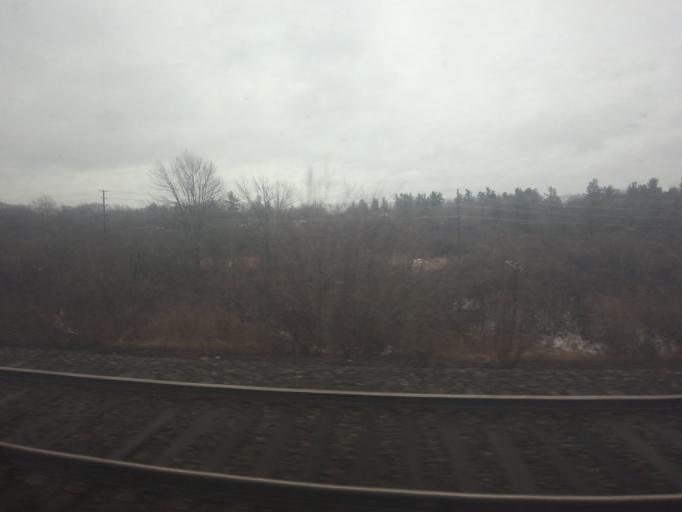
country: CA
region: Ontario
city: Kingston
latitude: 44.2902
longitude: -76.4505
